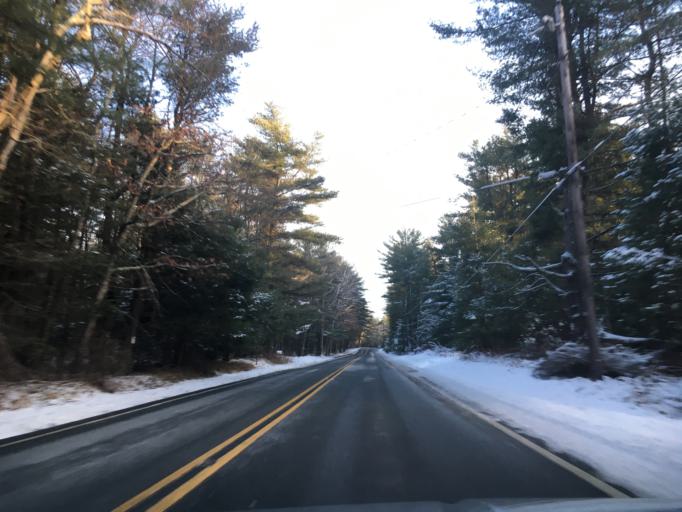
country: US
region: Pennsylvania
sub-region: Pike County
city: Hemlock Farms
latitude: 41.3265
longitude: -75.1231
